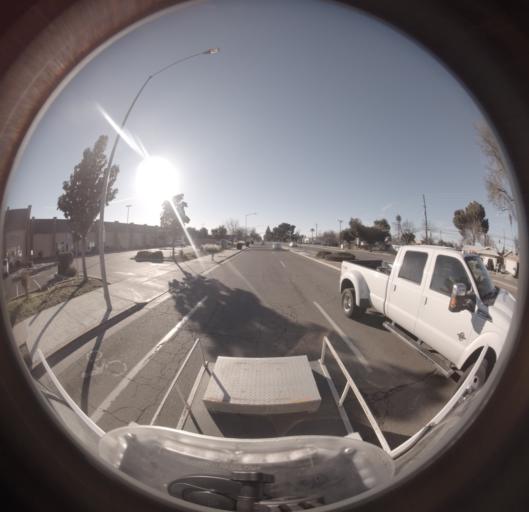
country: US
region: California
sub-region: Monterey County
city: King City
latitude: 36.1116
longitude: -120.9102
